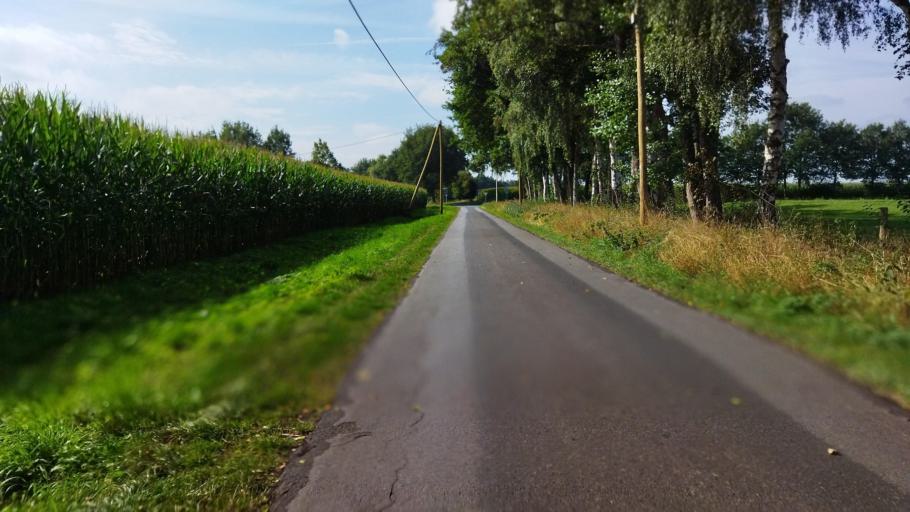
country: DE
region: North Rhine-Westphalia
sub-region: Regierungsbezirk Munster
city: Sassenberg
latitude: 51.9971
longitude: 8.0139
